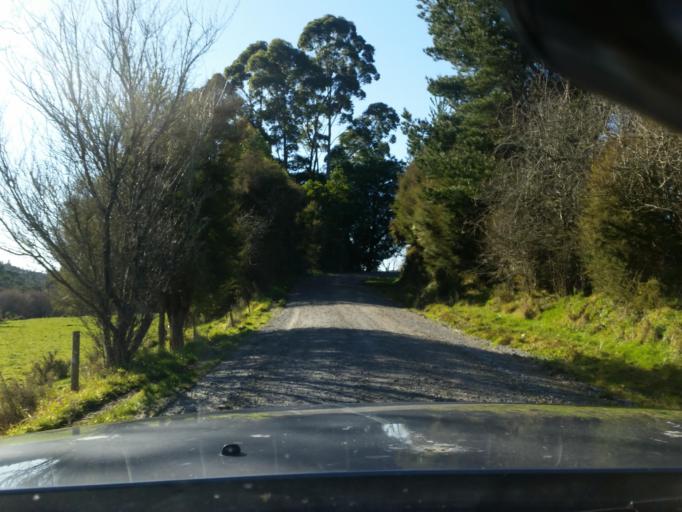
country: NZ
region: Tasman
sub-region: Tasman District
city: Takaka
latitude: -40.8418
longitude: 172.7794
